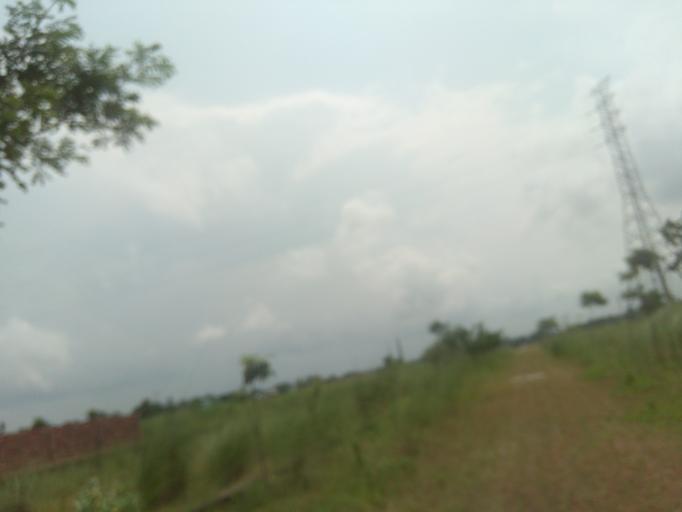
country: BD
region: Dhaka
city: Azimpur
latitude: 23.7501
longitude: 90.3344
